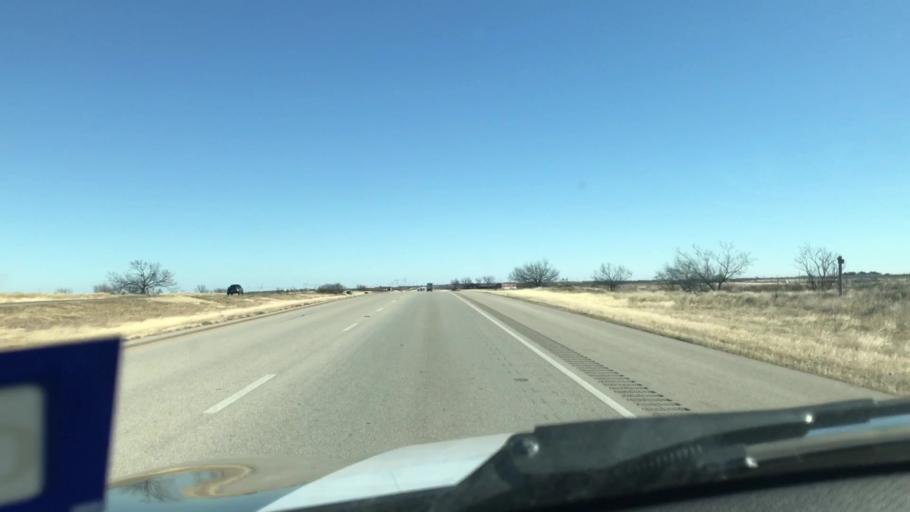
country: US
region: Texas
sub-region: Scurry County
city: Snyder
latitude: 32.6738
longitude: -100.8058
